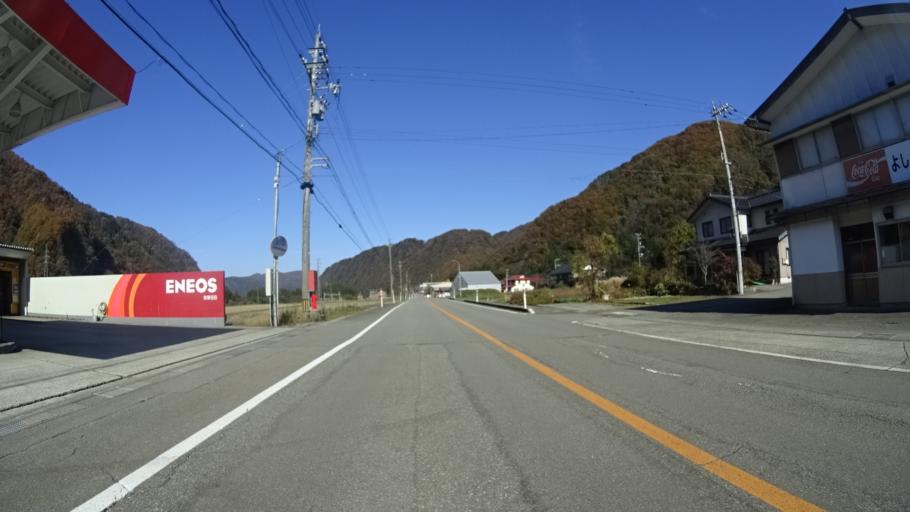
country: JP
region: Ishikawa
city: Tsurugi-asahimachi
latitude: 36.3478
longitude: 136.6273
